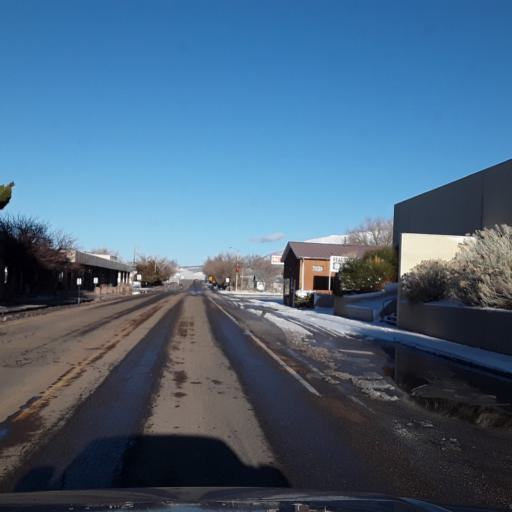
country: US
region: New Mexico
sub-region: Lincoln County
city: Carrizozo
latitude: 33.6432
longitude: -105.8758
